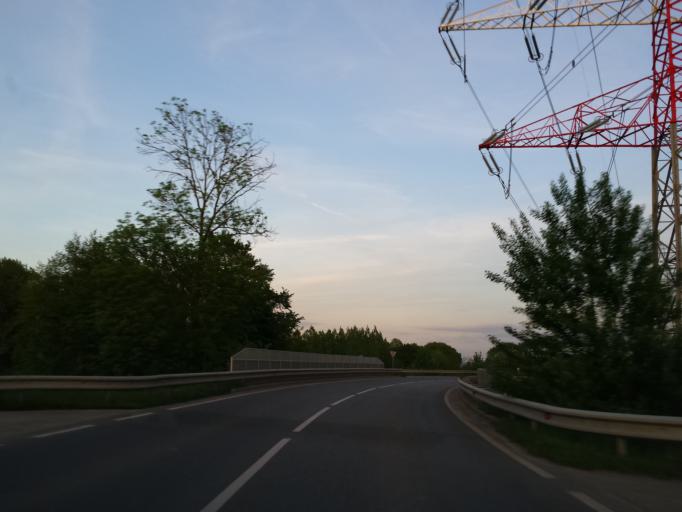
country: AT
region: Lower Austria
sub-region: Politischer Bezirk Tulln
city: Michelhausen
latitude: 48.3316
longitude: 15.9546
